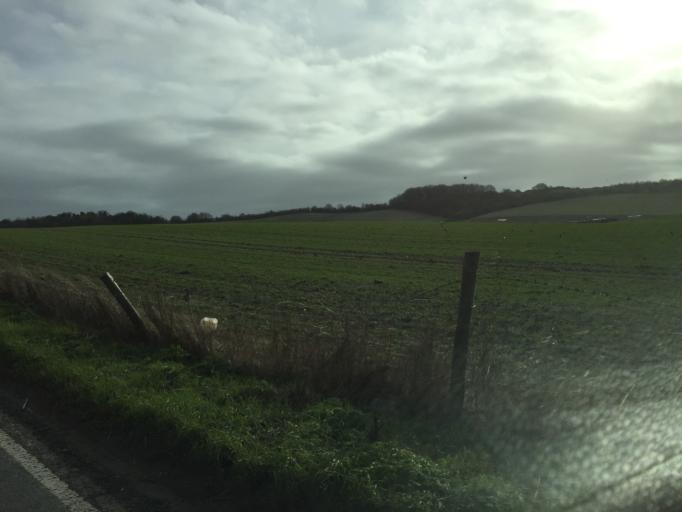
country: GB
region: England
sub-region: Oxfordshire
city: Cholsey
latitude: 51.5552
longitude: -1.1832
